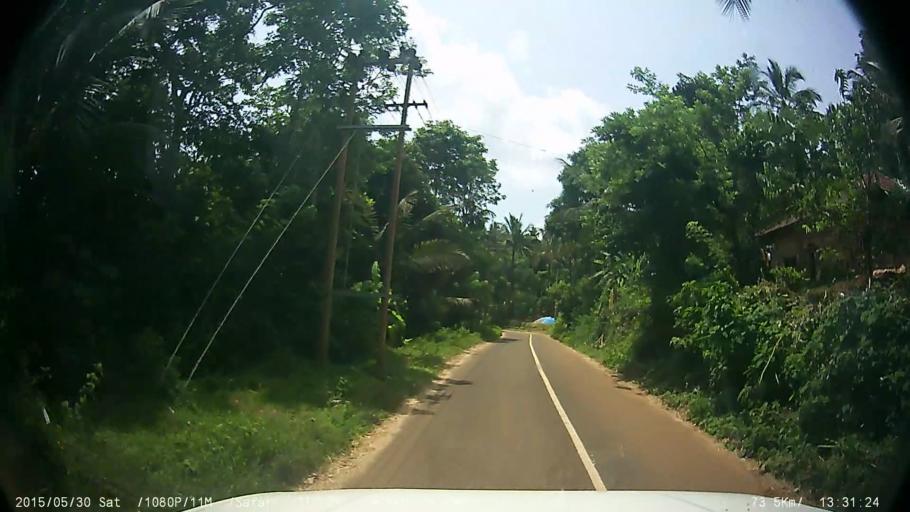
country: IN
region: Kerala
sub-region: Wayanad
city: Panamaram
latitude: 11.8151
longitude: 76.0836
